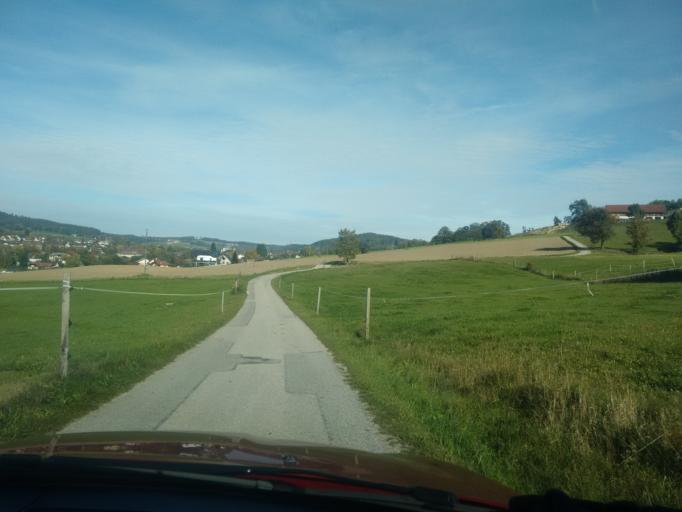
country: AT
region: Upper Austria
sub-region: Politischer Bezirk Vocklabruck
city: Zell am Pettenfirst
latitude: 48.0790
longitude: 13.5716
